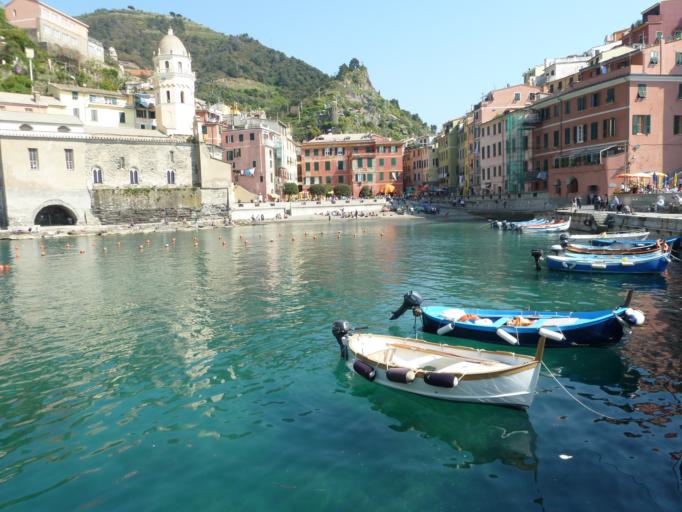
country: IT
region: Liguria
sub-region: Provincia di La Spezia
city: Vernazza
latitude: 44.1354
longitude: 9.6815
